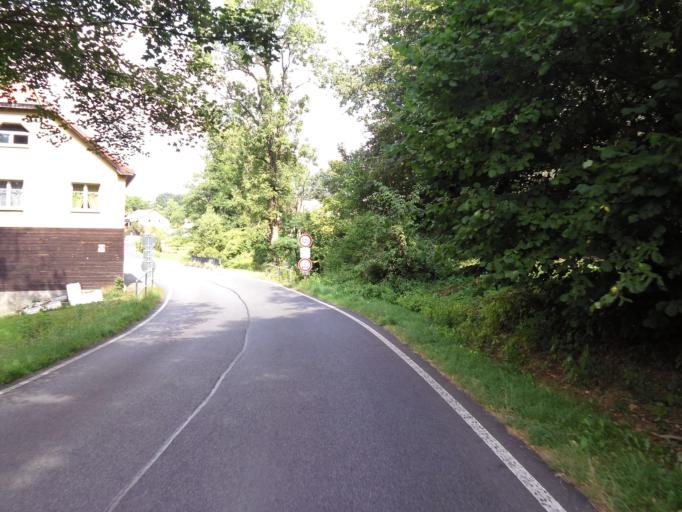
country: CZ
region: Liberecky
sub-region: Okres Ceska Lipa
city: Straz pod Ralskem
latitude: 50.7087
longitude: 14.8604
